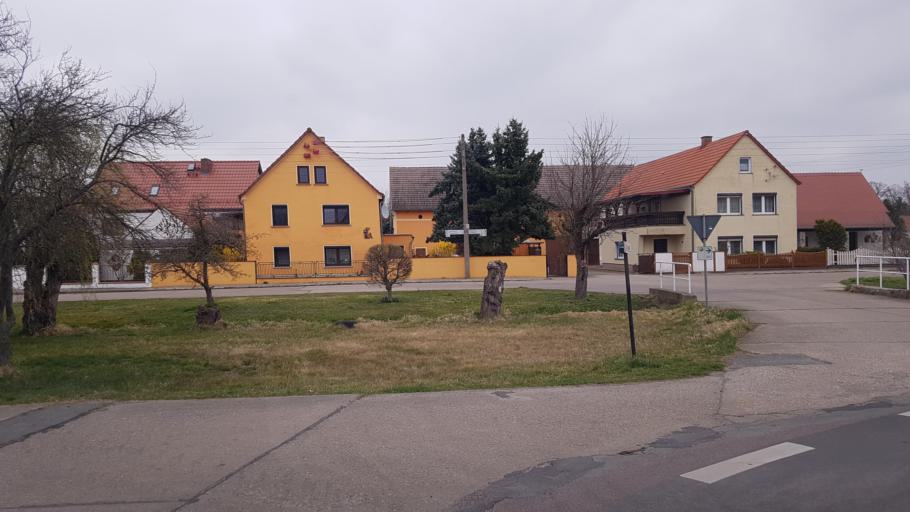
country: DE
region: Saxony
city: Nauwalde
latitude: 51.4212
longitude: 13.3889
